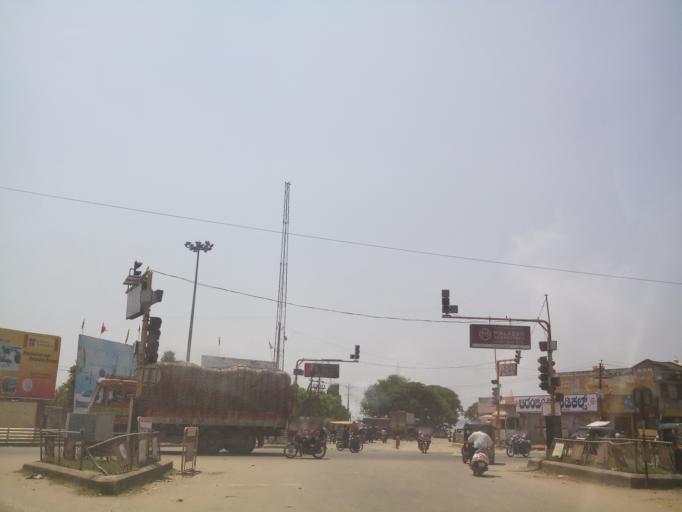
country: IN
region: Karnataka
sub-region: Hassan
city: Hassan
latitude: 13.0006
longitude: 76.0940
